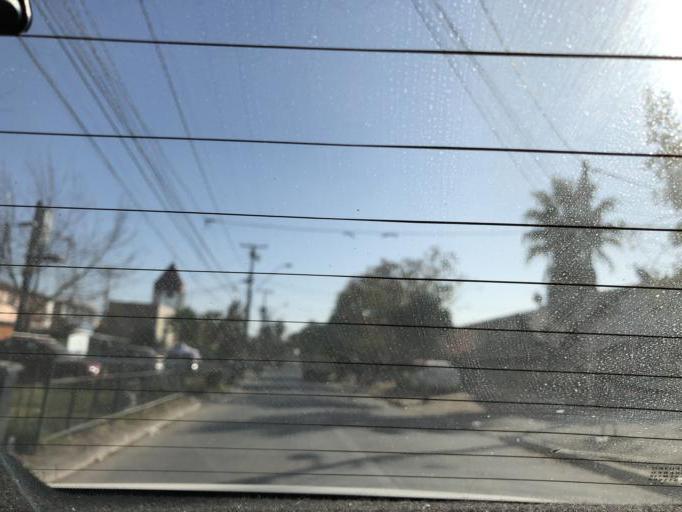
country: CL
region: Santiago Metropolitan
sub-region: Provincia de Cordillera
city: Puente Alto
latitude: -33.6210
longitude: -70.5948
